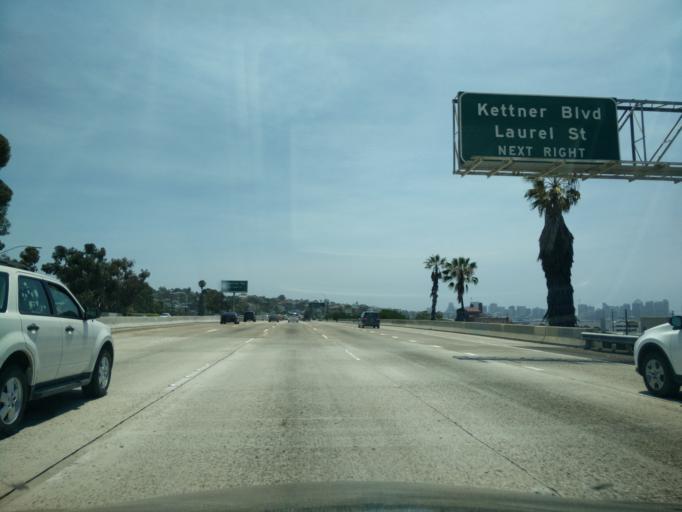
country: US
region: California
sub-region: San Diego County
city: San Diego
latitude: 32.7444
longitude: -117.1869
